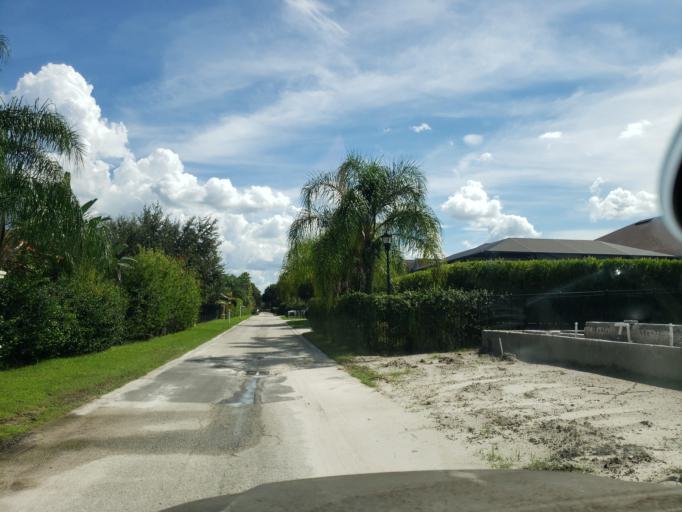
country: US
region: Florida
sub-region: Hillsborough County
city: Fish Hawk
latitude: 27.8451
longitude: -82.2114
